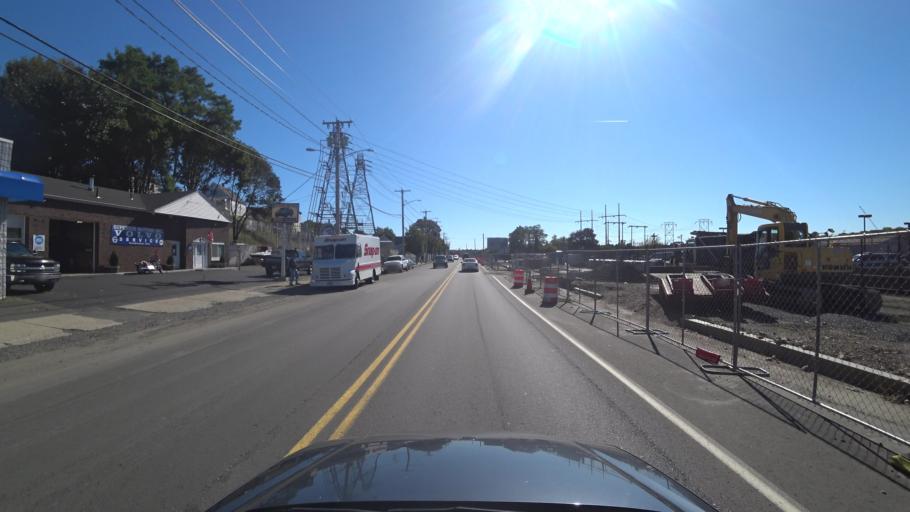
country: US
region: Massachusetts
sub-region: Essex County
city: Salem
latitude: 42.5157
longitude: -70.8959
